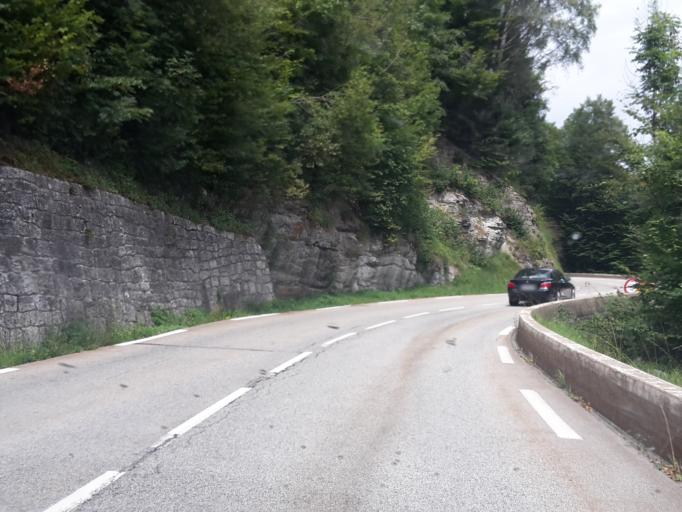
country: FR
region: Rhone-Alpes
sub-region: Departement de la Haute-Savoie
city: Praz-sur-Arly
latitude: 45.8037
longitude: 6.4976
